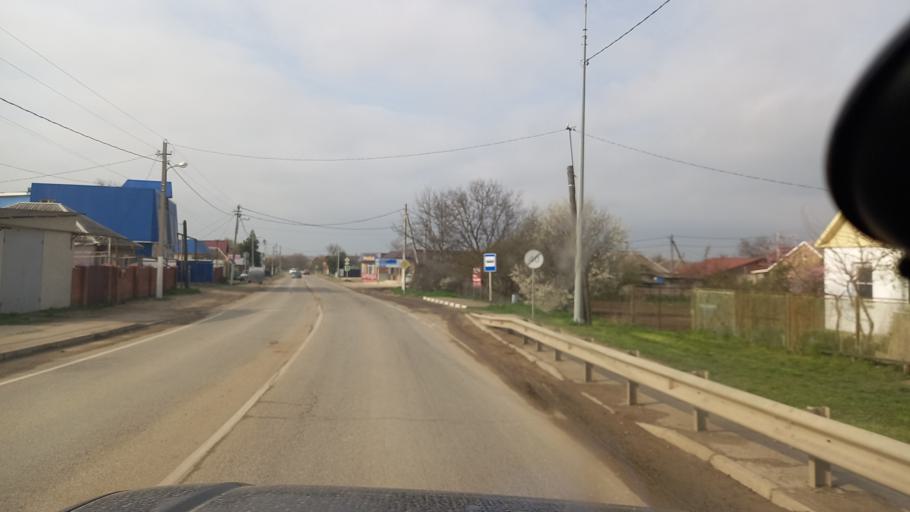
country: RU
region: Krasnodarskiy
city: Varenikovskaya
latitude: 45.1100
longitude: 37.6400
